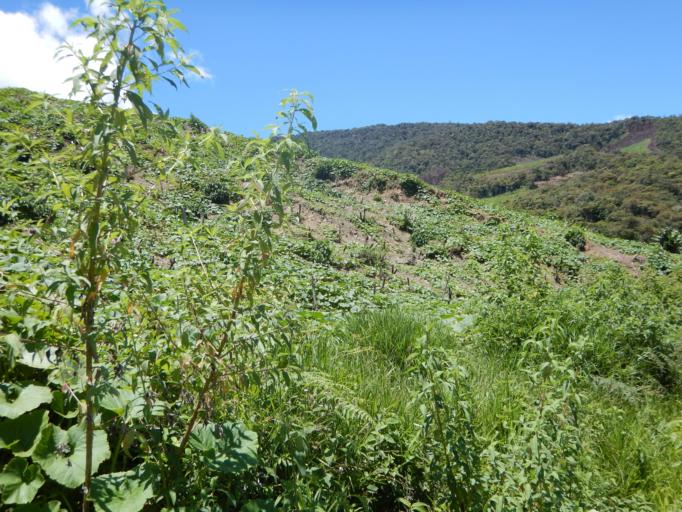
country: BO
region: La Paz
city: Coroico
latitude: -16.2819
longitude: -67.7120
